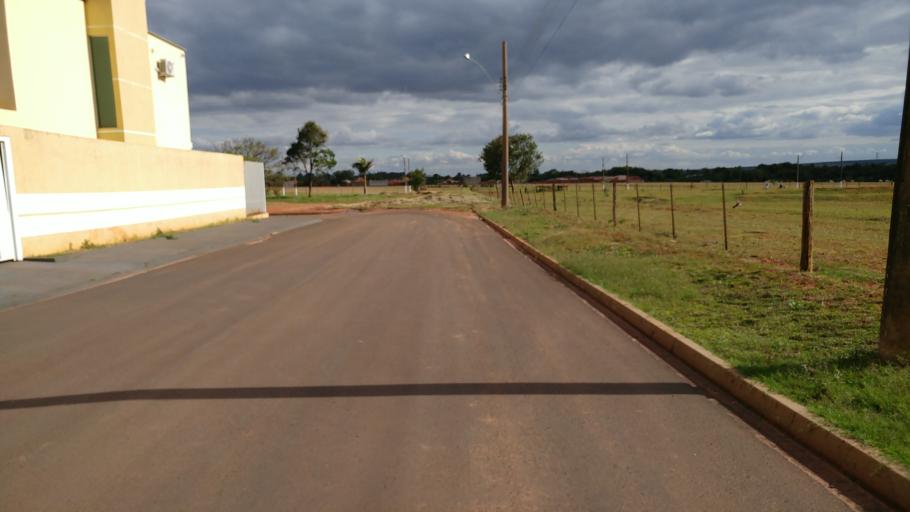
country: BR
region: Sao Paulo
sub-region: Paraguacu Paulista
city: Paraguacu Paulista
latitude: -22.4088
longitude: -50.5925
